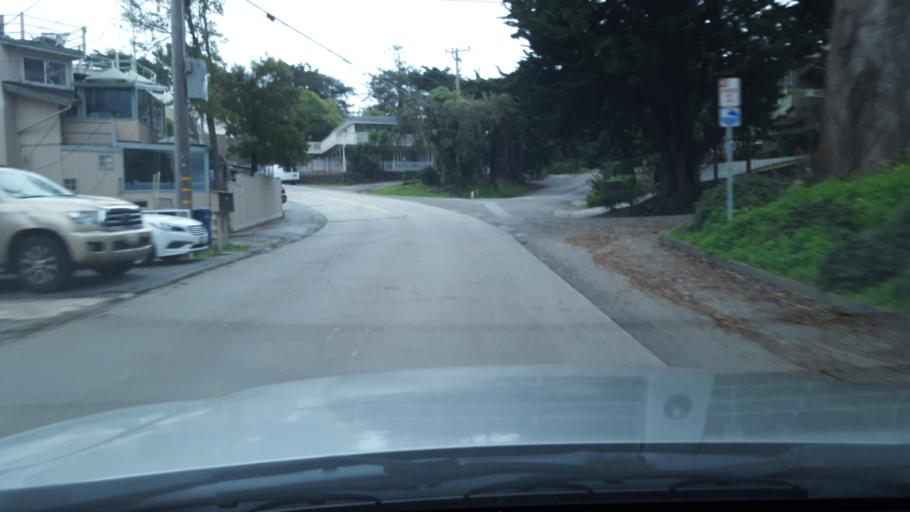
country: US
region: California
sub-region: Santa Cruz County
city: Rio Del Mar
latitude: 36.9682
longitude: -121.9013
